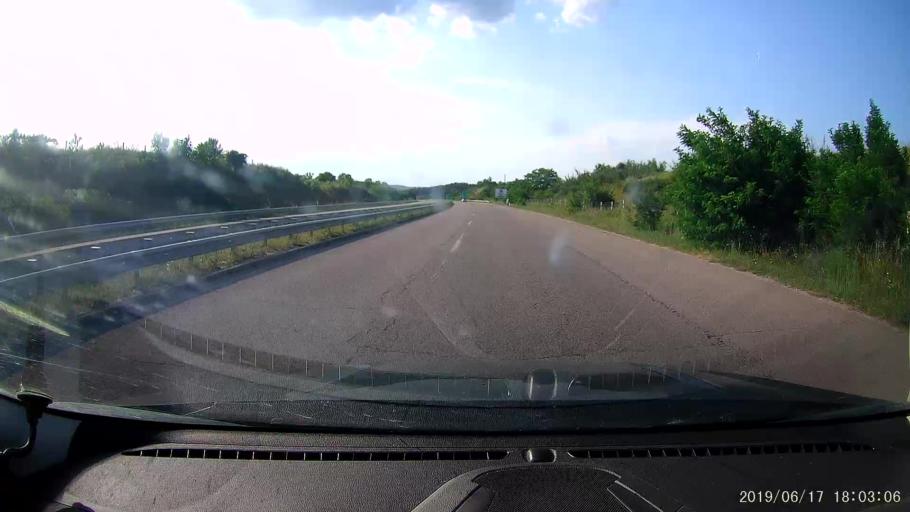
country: BG
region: Khaskovo
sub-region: Obshtina Svilengrad
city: Svilengrad
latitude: 41.7721
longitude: 26.2241
